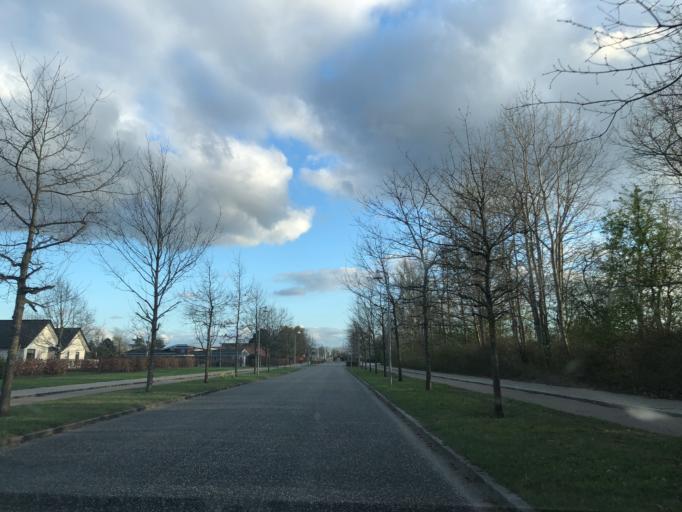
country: DK
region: Zealand
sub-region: Ringsted Kommune
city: Ringsted
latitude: 55.4469
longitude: 11.8107
